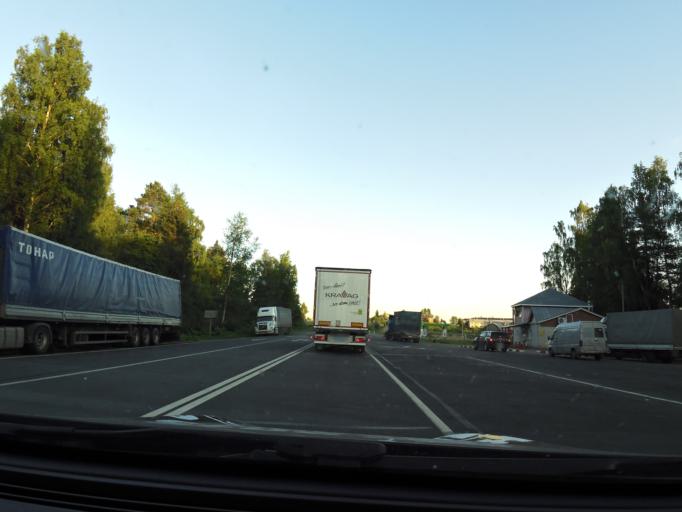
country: RU
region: Jaroslavl
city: Prechistoye
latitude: 58.4366
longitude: 40.3214
